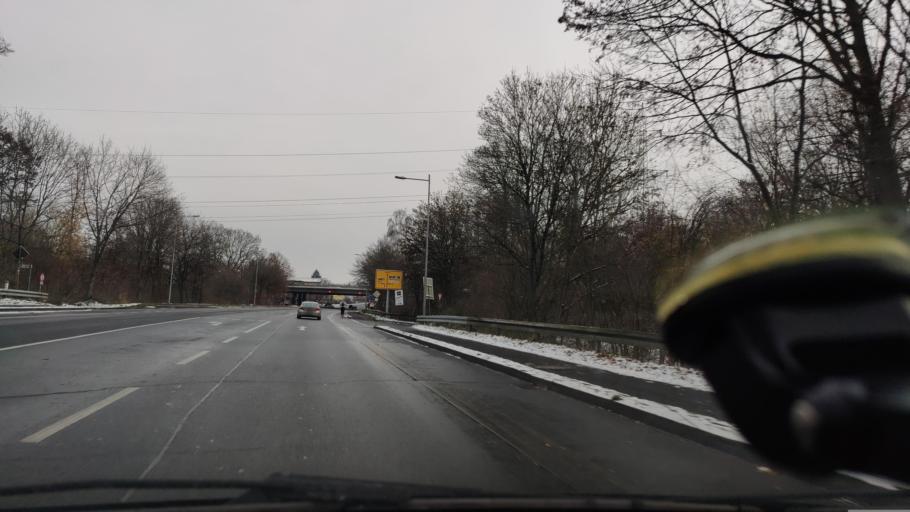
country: DE
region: North Rhine-Westphalia
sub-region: Regierungsbezirk Koln
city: Siegburg
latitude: 50.8119
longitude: 7.1851
